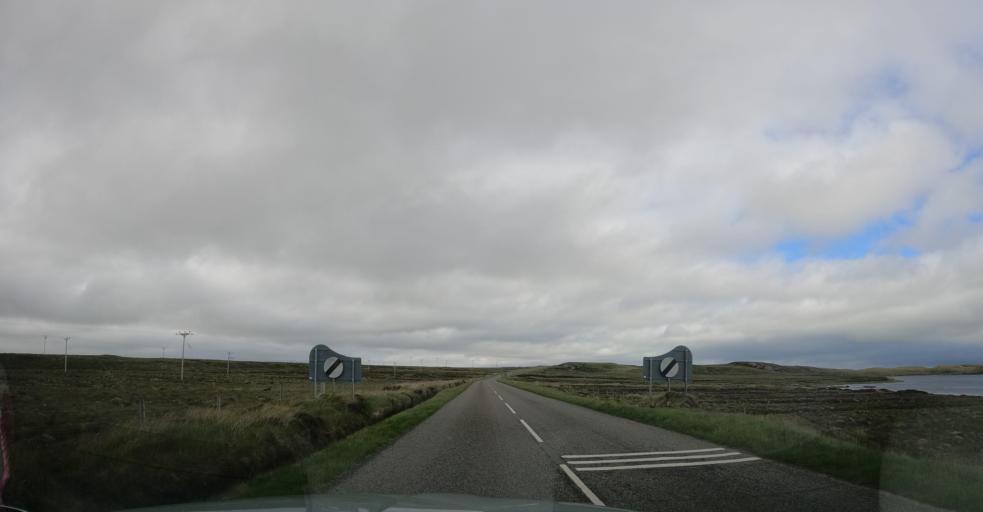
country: GB
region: Scotland
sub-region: Eilean Siar
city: Stornoway
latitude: 58.1597
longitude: -6.4951
